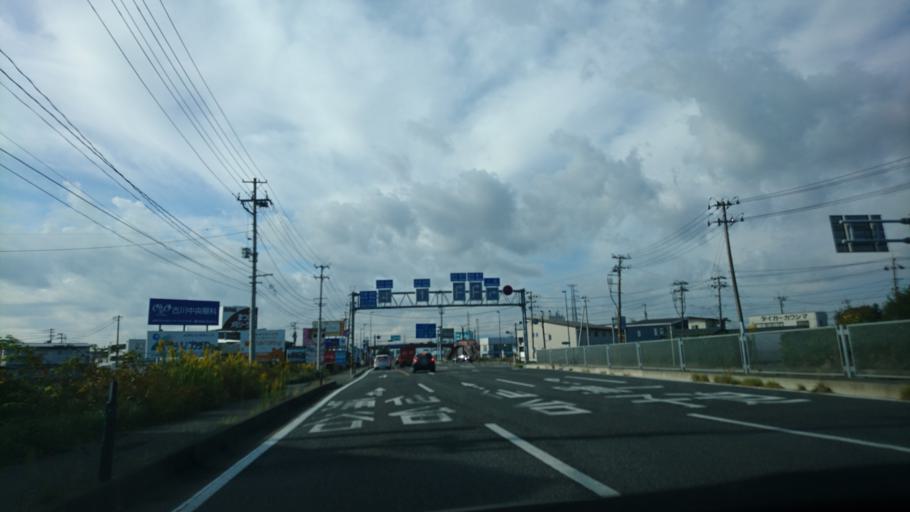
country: JP
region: Miyagi
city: Furukawa
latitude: 38.5856
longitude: 140.9496
